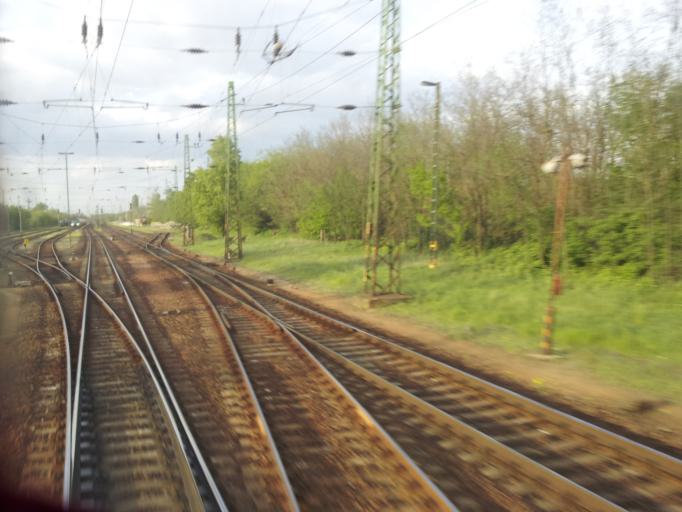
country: HU
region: Pest
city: Dunakeszi
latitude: 47.6180
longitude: 19.1331
